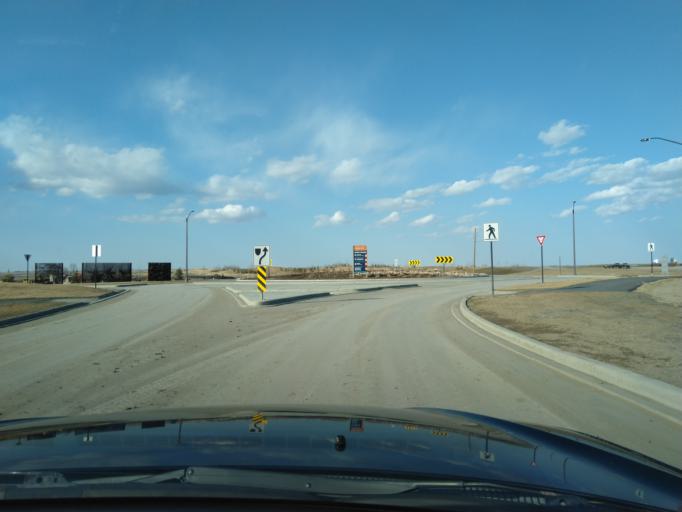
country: CA
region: Alberta
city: Cochrane
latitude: 51.1199
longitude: -114.3876
